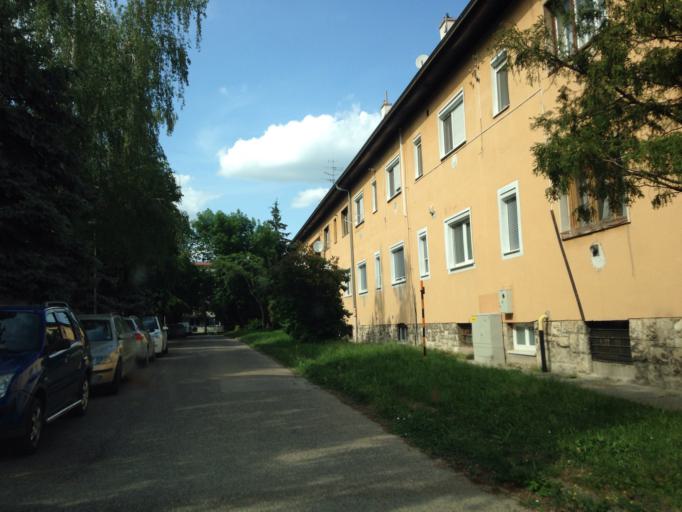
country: SK
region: Nitriansky
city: Komarno
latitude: 47.7607
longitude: 18.1377
